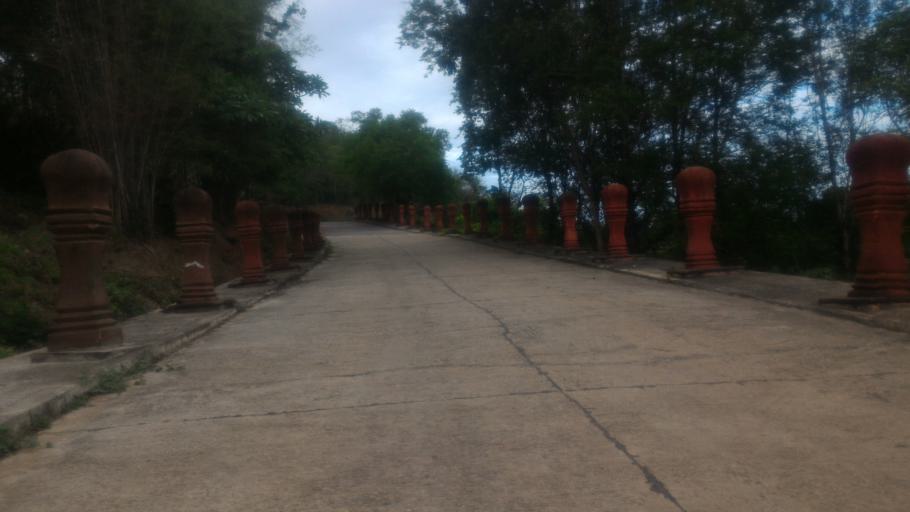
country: TH
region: Prachuap Khiri Khan
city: Kui Buri
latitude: 12.1086
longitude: 99.7551
